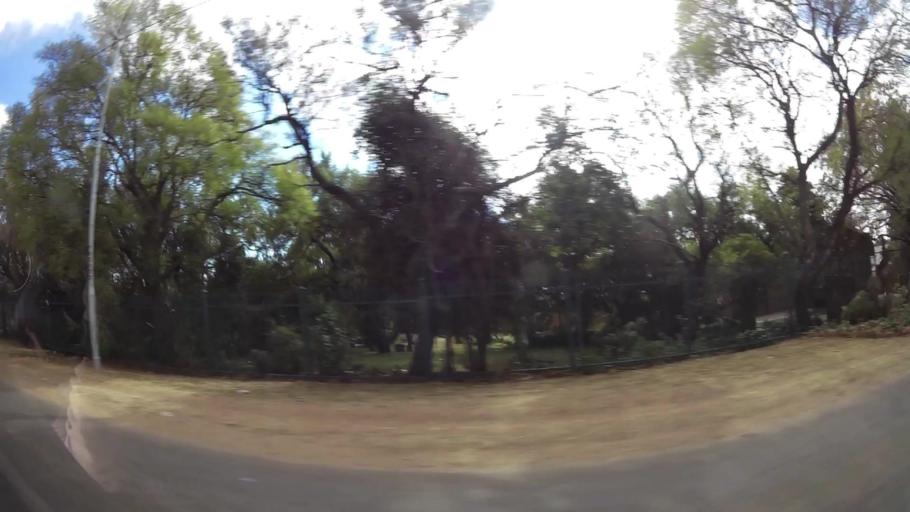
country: ZA
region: Gauteng
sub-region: West Rand District Municipality
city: Muldersdriseloop
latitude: -26.0947
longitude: 27.8650
